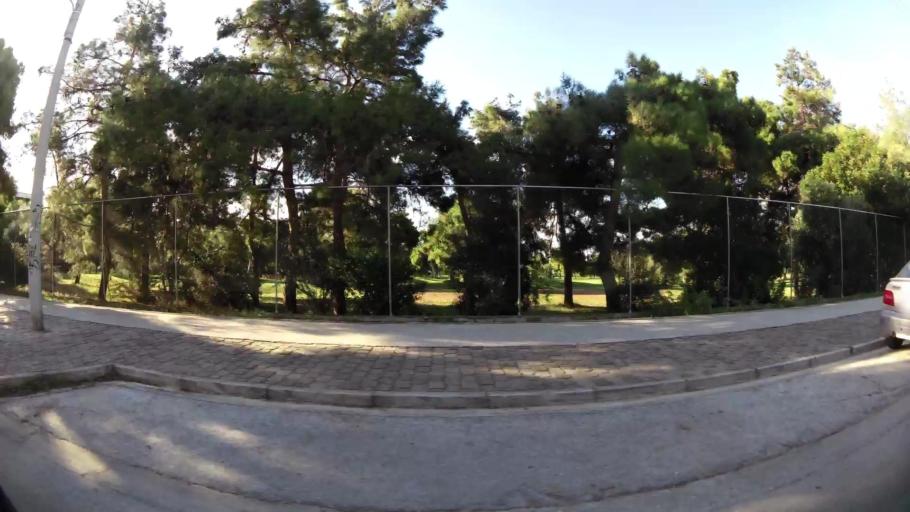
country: GR
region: Attica
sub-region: Nomarchia Athinas
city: Glyfada
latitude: 37.8742
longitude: 23.7500
